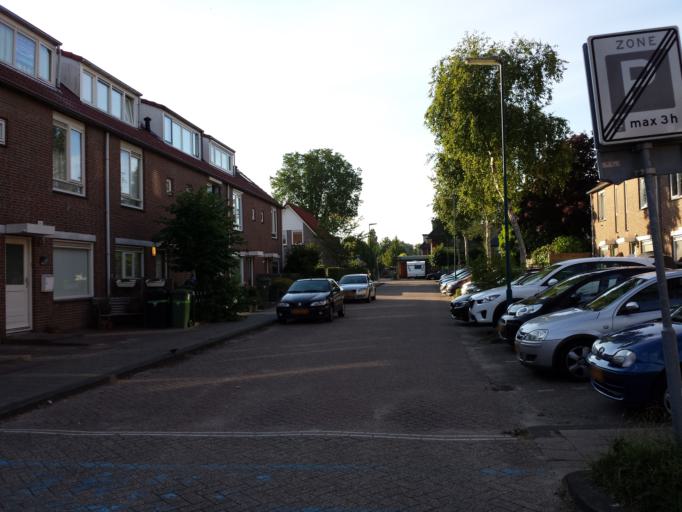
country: NL
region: South Holland
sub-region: Gemeente Zoetermeer
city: Zoetermeer
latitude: 52.0444
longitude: 4.4867
